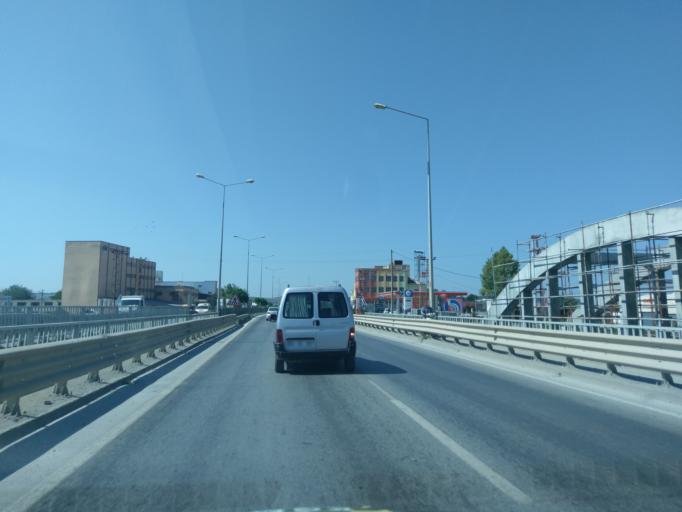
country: TR
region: Samsun
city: Bafra
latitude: 41.5675
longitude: 35.8804
